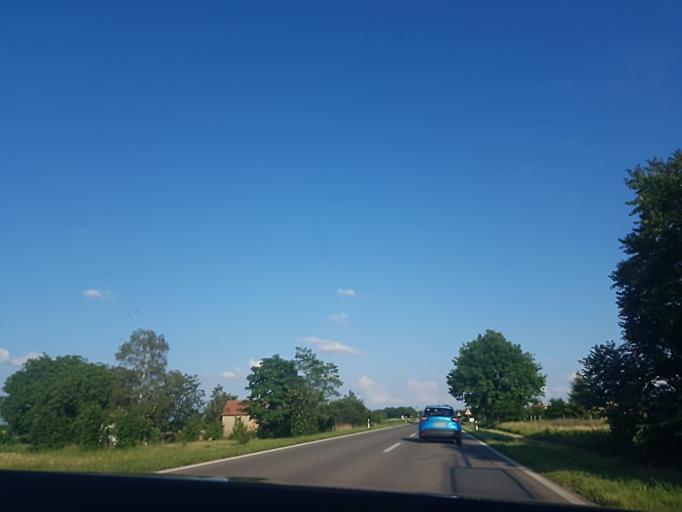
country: RS
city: Banatski Karlovac
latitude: 45.0585
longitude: 20.9919
